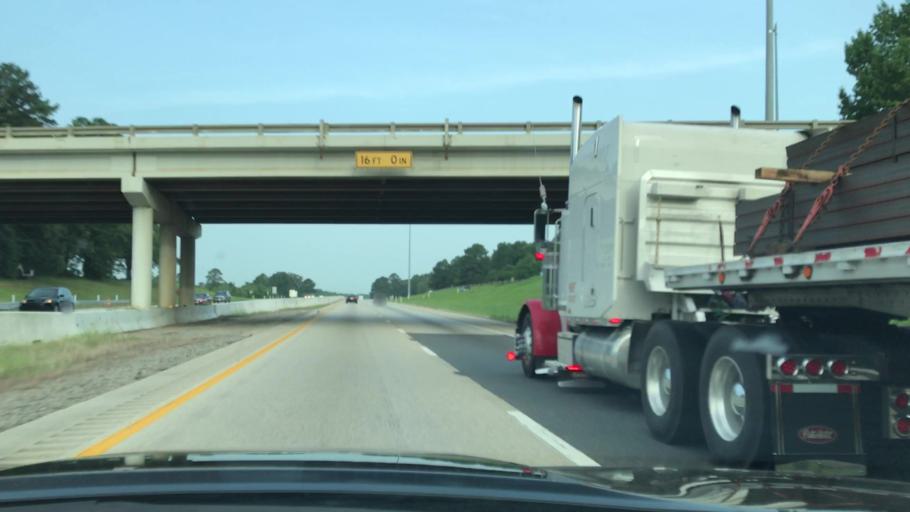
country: US
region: Texas
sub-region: Gregg County
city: Kilgore
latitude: 32.4329
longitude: -94.8619
